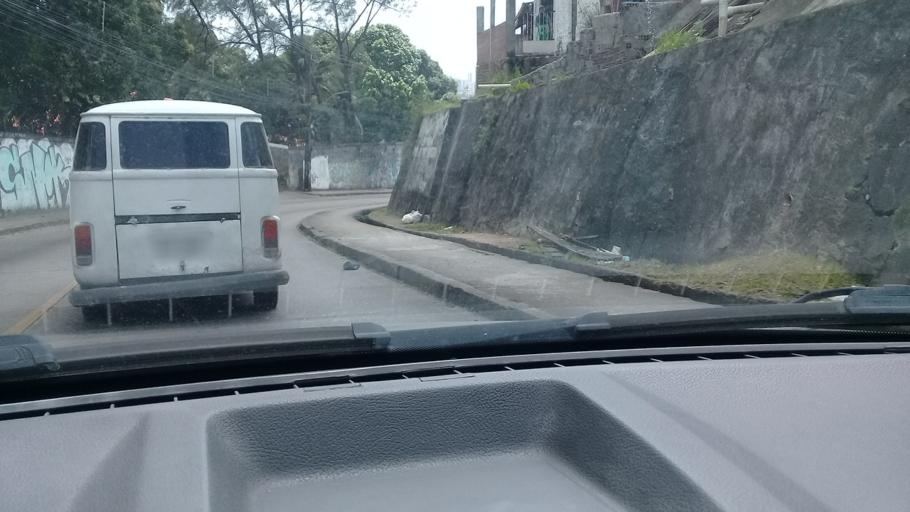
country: BR
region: Pernambuco
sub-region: Jaboatao Dos Guararapes
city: Jaboatao dos Guararapes
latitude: -8.1183
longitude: -34.9453
